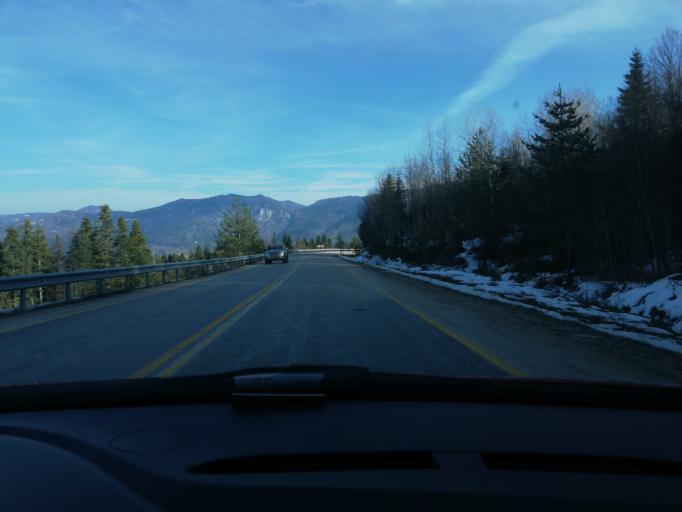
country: TR
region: Kastamonu
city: Senpazar
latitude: 41.7875
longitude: 33.1378
